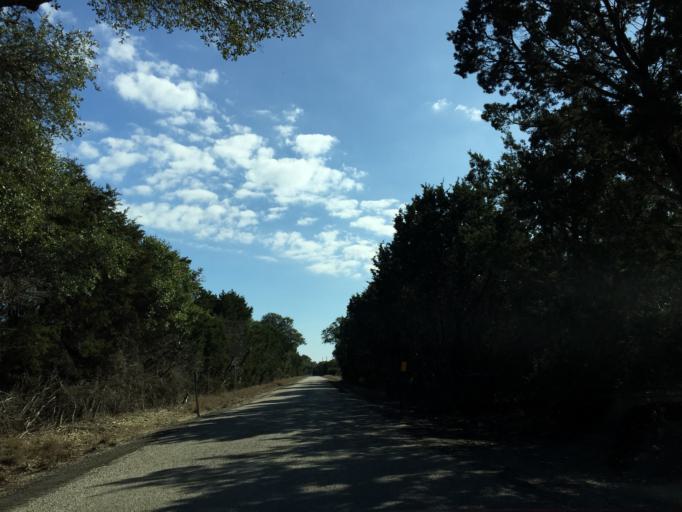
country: US
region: Texas
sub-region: Williamson County
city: Florence
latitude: 30.7776
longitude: -97.8906
